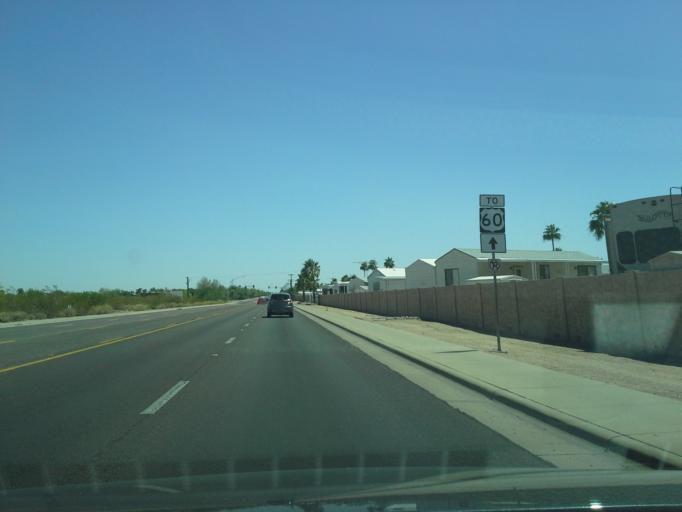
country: US
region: Arizona
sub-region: Pinal County
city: Apache Junction
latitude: 33.4109
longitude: -111.5462
